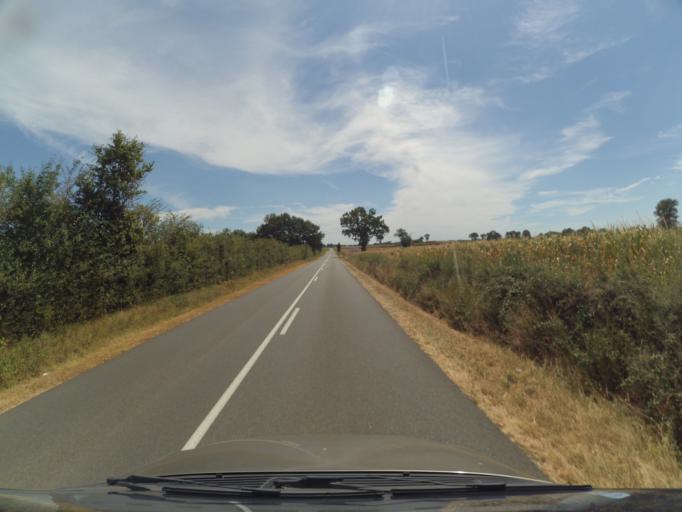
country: FR
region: Poitou-Charentes
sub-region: Departement de la Vienne
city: Availles-Limouzine
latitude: 46.1304
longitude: 0.5588
